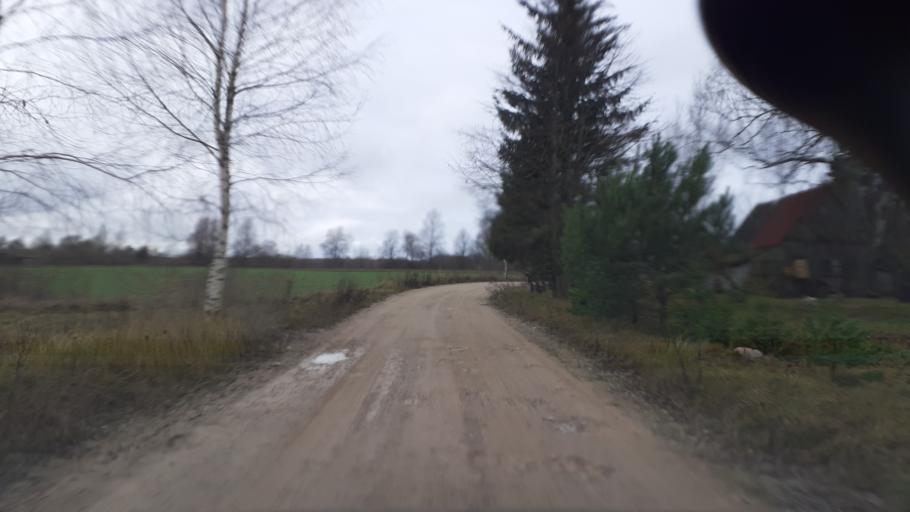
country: LV
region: Kuldigas Rajons
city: Kuldiga
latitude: 57.0431
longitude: 21.8728
